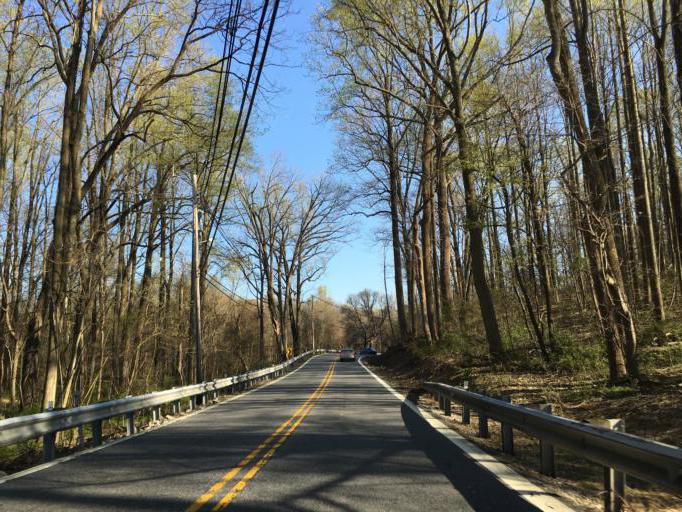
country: US
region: Maryland
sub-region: Baltimore County
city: Perry Hall
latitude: 39.4304
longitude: -76.4908
